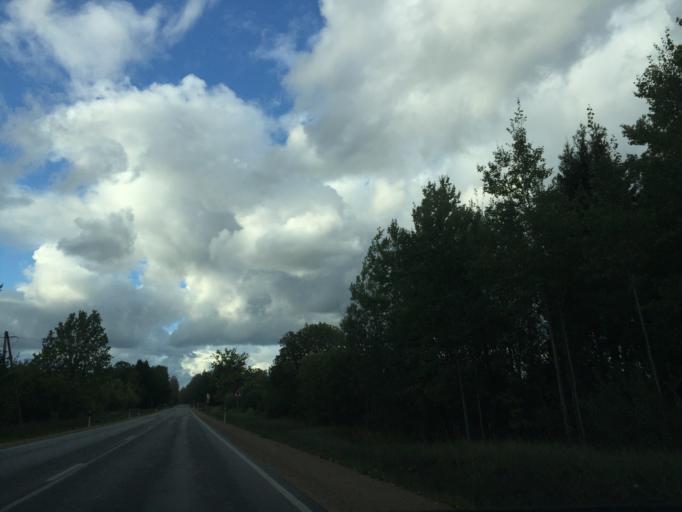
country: LV
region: Ligatne
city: Ligatne
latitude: 57.1747
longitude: 25.0414
